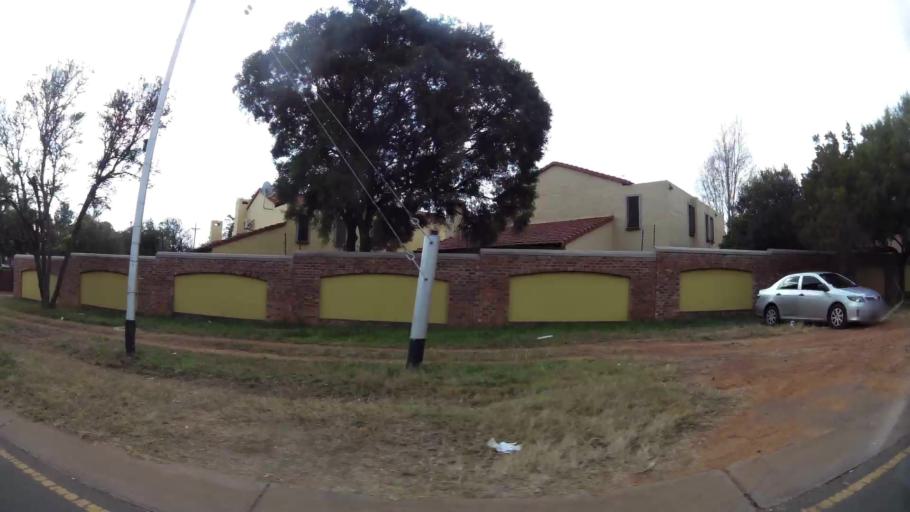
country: ZA
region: Gauteng
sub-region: City of Tshwane Metropolitan Municipality
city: Pretoria
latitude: -25.7785
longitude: 28.2882
